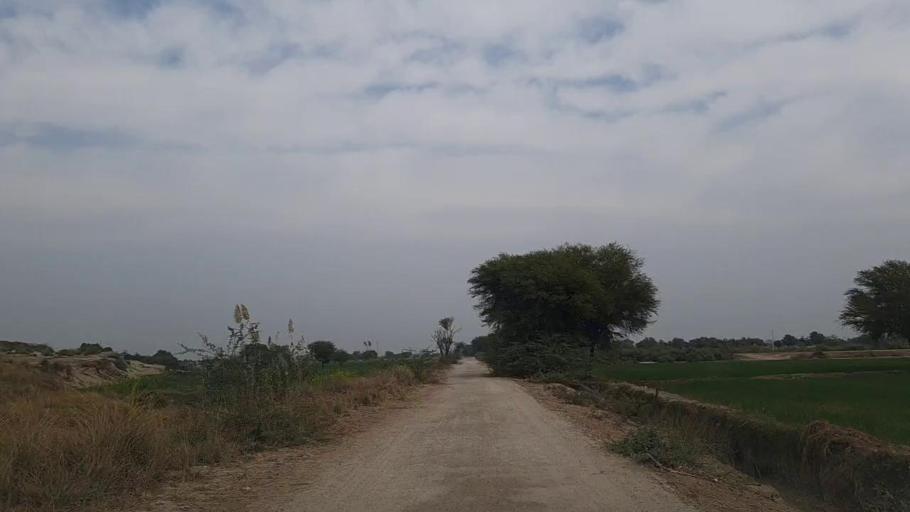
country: PK
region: Sindh
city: Daur
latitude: 26.4267
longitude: 68.4619
